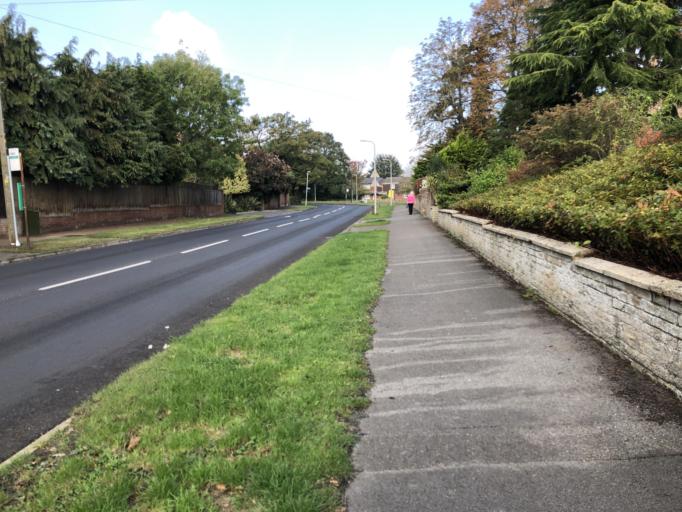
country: GB
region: England
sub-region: West Berkshire
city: Tilehurst
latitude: 51.4485
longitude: -1.0301
